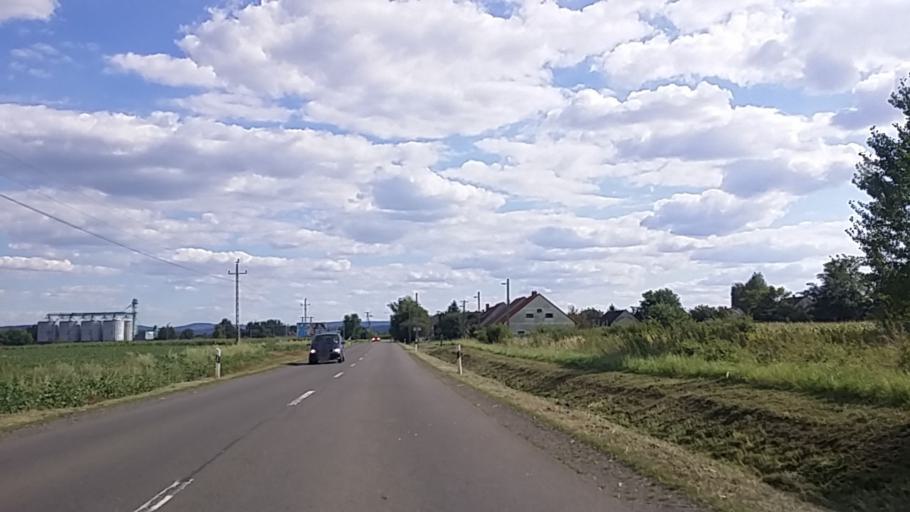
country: HU
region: Baranya
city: Sasd
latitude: 46.2672
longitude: 18.1043
